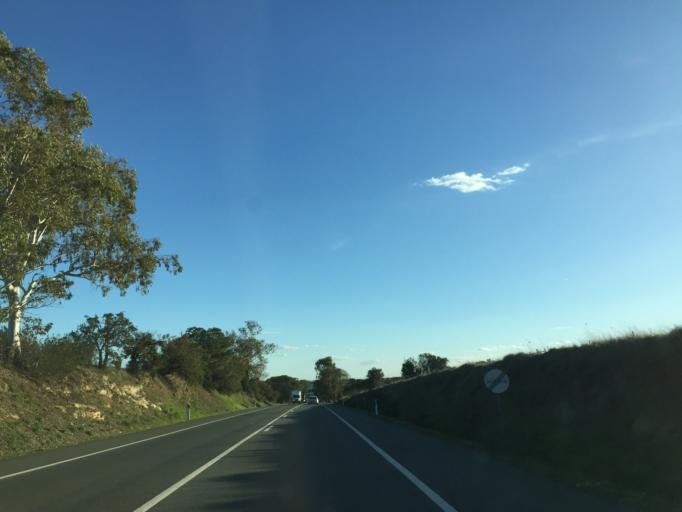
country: PT
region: Setubal
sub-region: Grandola
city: Grandola
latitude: 38.0930
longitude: -8.4184
